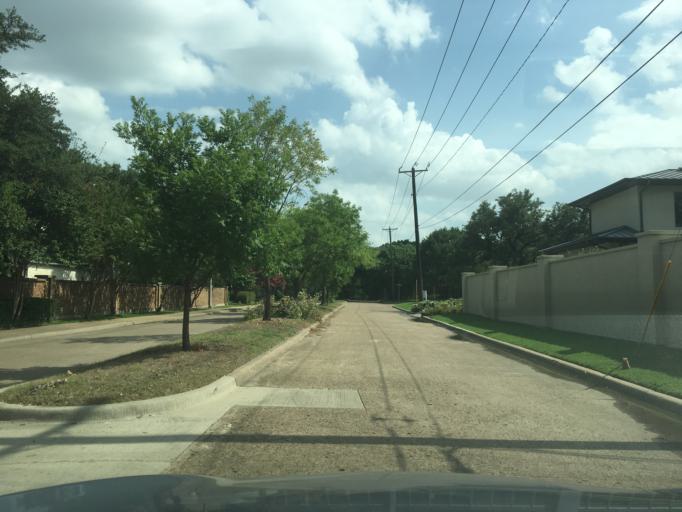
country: US
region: Texas
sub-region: Dallas County
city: University Park
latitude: 32.8921
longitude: -96.8126
